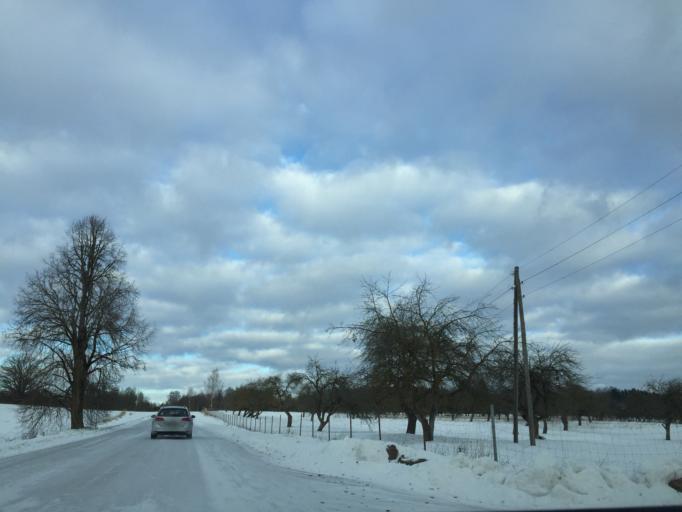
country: LV
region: Lielvarde
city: Lielvarde
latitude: 56.5664
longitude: 24.7339
